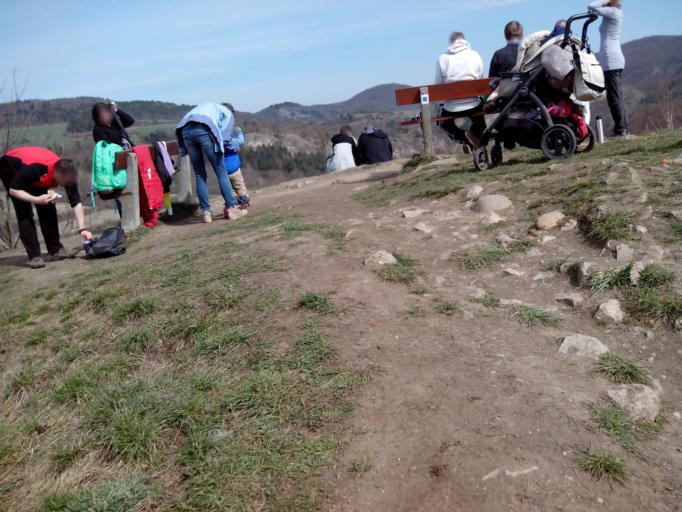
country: CZ
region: Central Bohemia
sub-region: Okres Beroun
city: Beroun
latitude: 49.9501
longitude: 14.1065
